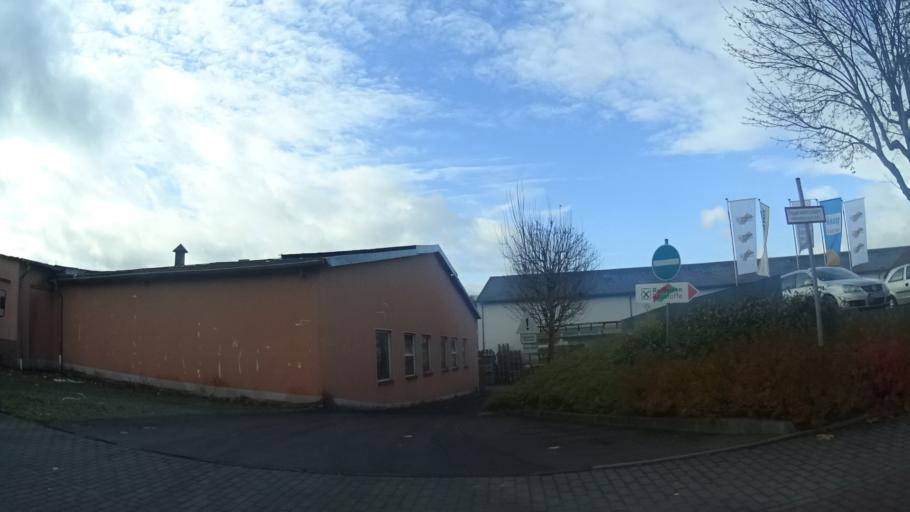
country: DE
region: Hesse
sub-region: Regierungsbezirk Kassel
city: Hunfeld
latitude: 50.6667
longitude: 9.7617
